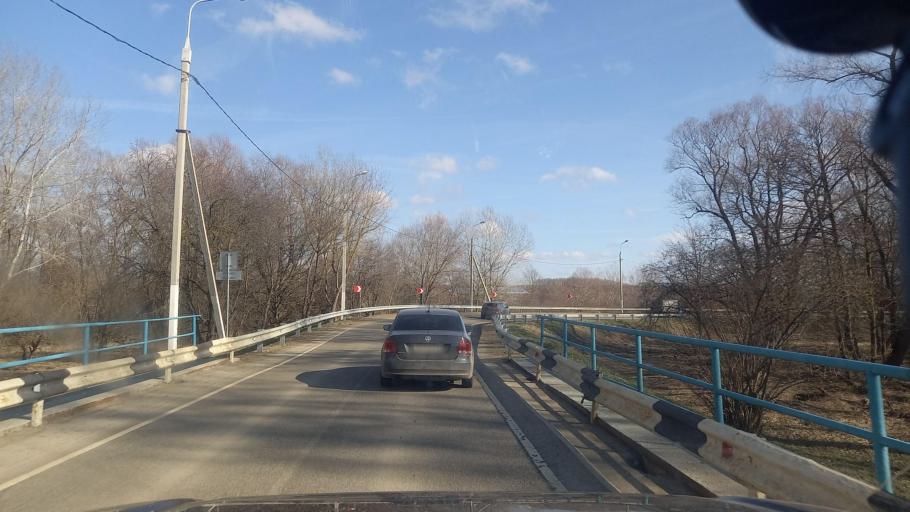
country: RU
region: Krasnodarskiy
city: Novodmitriyevskaya
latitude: 44.7771
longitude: 38.9753
